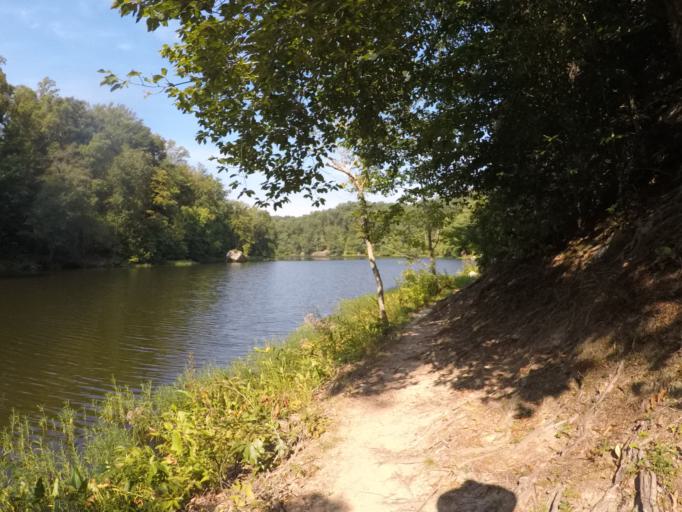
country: US
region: Ohio
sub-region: Lawrence County
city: Ironton
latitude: 38.6084
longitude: -82.6265
